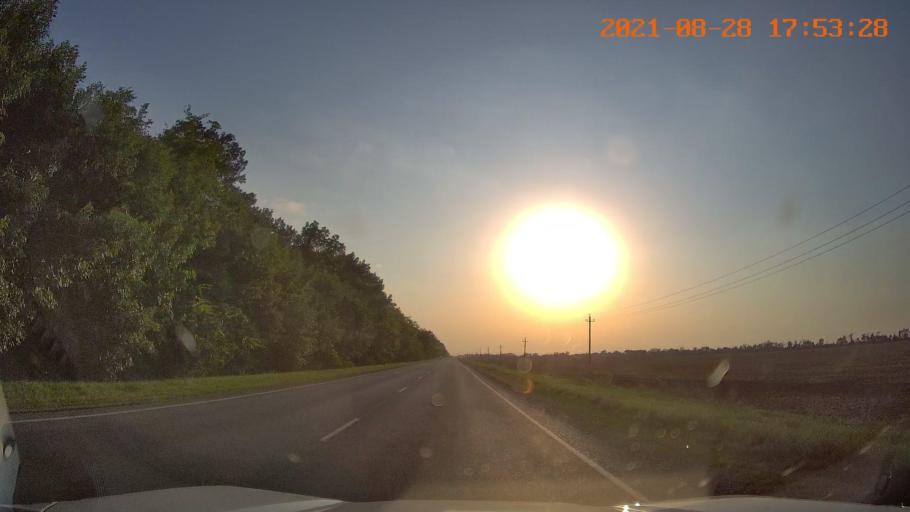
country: RU
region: Krasnodarskiy
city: Konstantinovskaya
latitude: 44.9383
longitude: 40.7587
